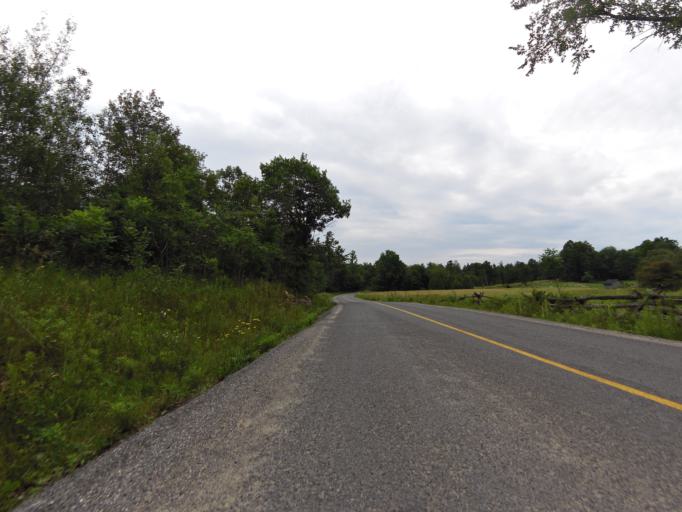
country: CA
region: Ontario
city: Perth
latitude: 44.6699
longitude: -76.6588
